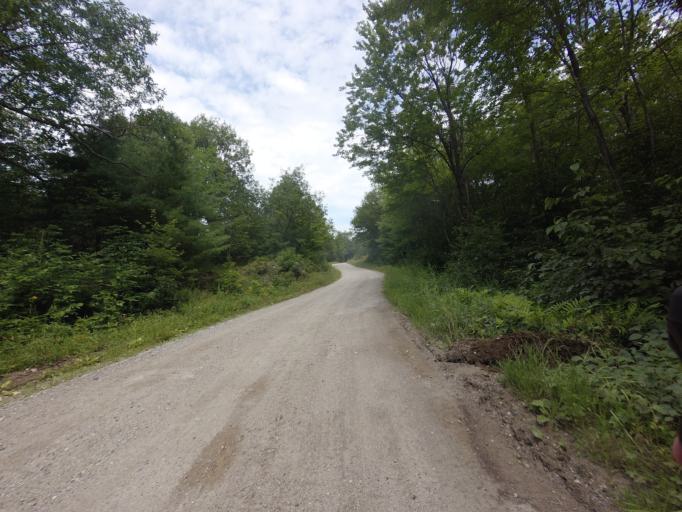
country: CA
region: Ontario
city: Perth
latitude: 44.7675
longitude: -76.6149
